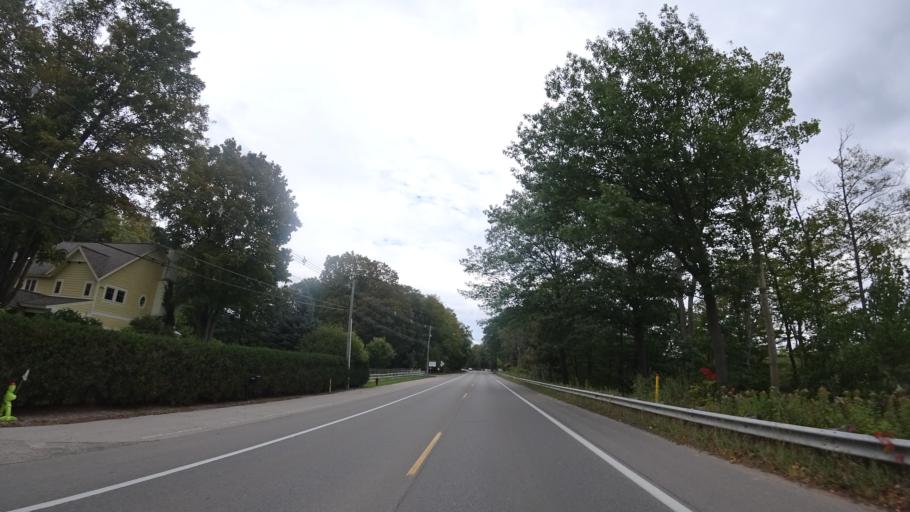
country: US
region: Michigan
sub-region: Emmet County
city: Harbor Springs
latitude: 45.4318
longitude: -84.9673
